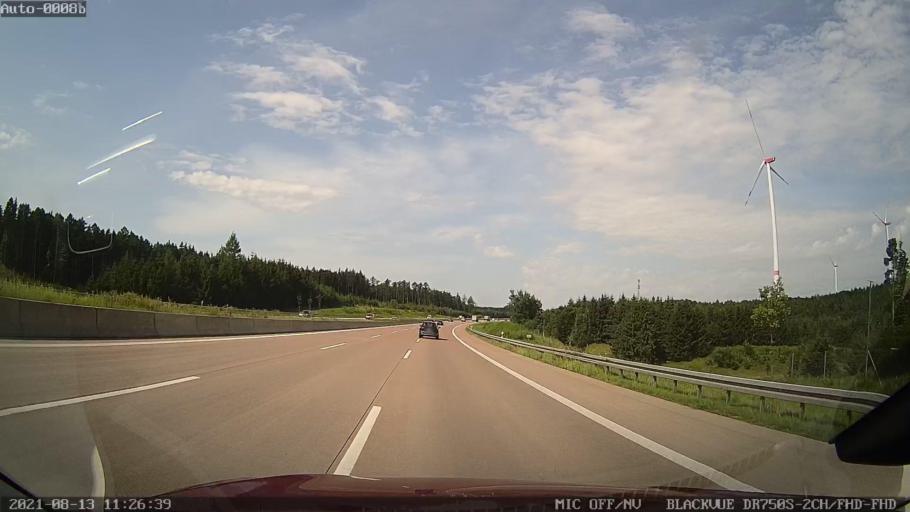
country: DE
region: Bavaria
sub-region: Swabia
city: Landensberg
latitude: 48.4005
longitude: 10.5486
